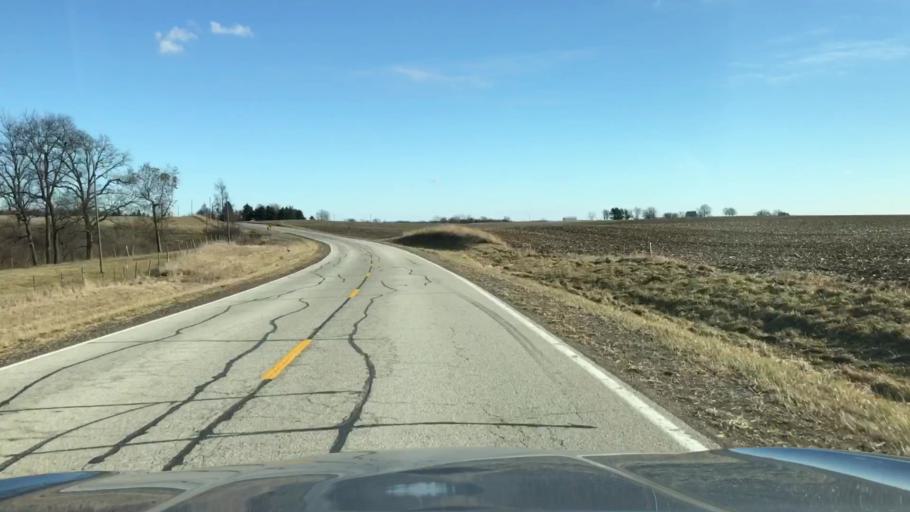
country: US
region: Illinois
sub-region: McLean County
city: Lexington
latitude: 40.6490
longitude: -88.8746
